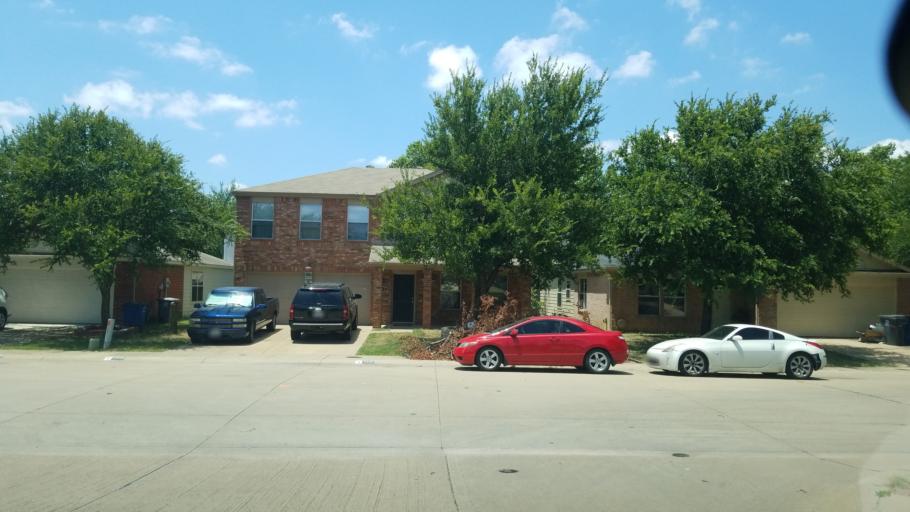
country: US
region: Texas
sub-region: Dallas County
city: Balch Springs
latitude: 32.7472
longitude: -96.7006
